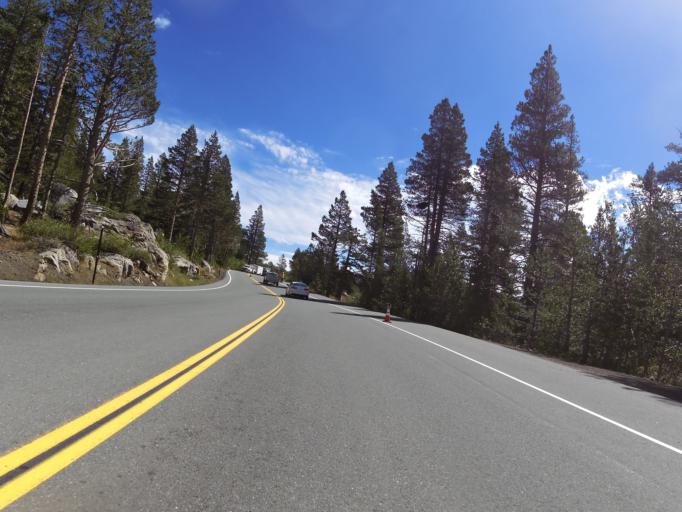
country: US
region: California
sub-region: El Dorado County
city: South Lake Tahoe
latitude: 38.6997
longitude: -120.0299
